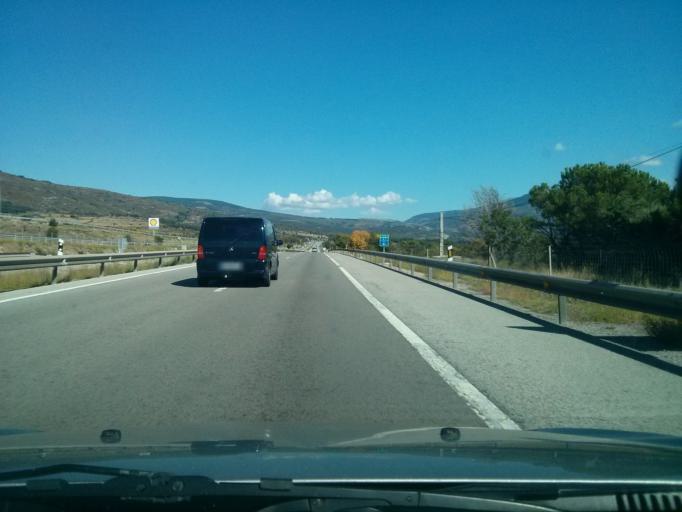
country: ES
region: Madrid
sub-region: Provincia de Madrid
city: Braojos
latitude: 41.0399
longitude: -3.6170
